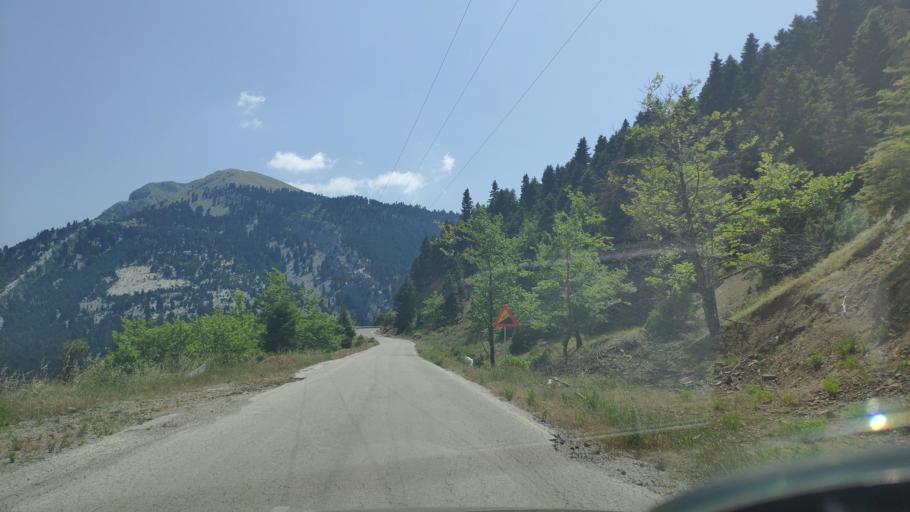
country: GR
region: Epirus
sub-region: Nomos Artas
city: Ano Kalentini
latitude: 39.2751
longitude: 21.2840
